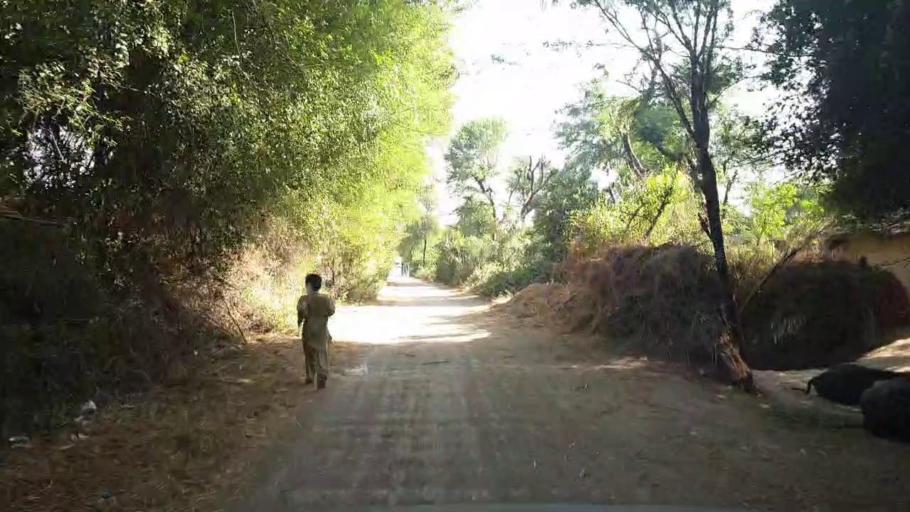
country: PK
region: Sindh
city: Matli
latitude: 25.0266
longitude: 68.7334
